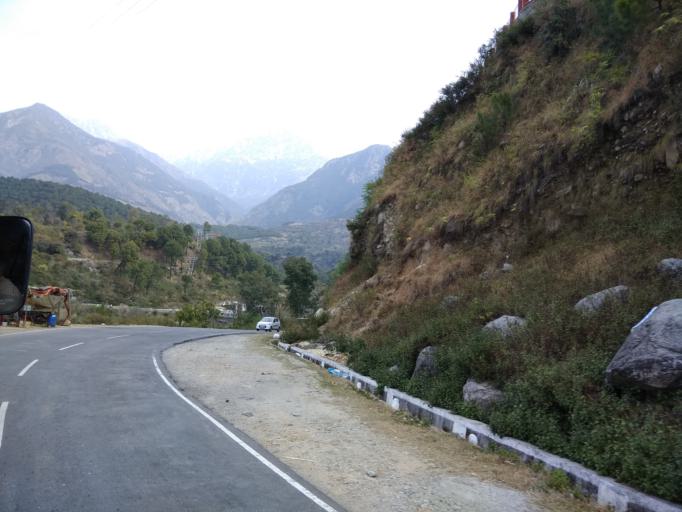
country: IN
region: Himachal Pradesh
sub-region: Kangra
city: Dharmsala
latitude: 32.1594
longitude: 76.4059
